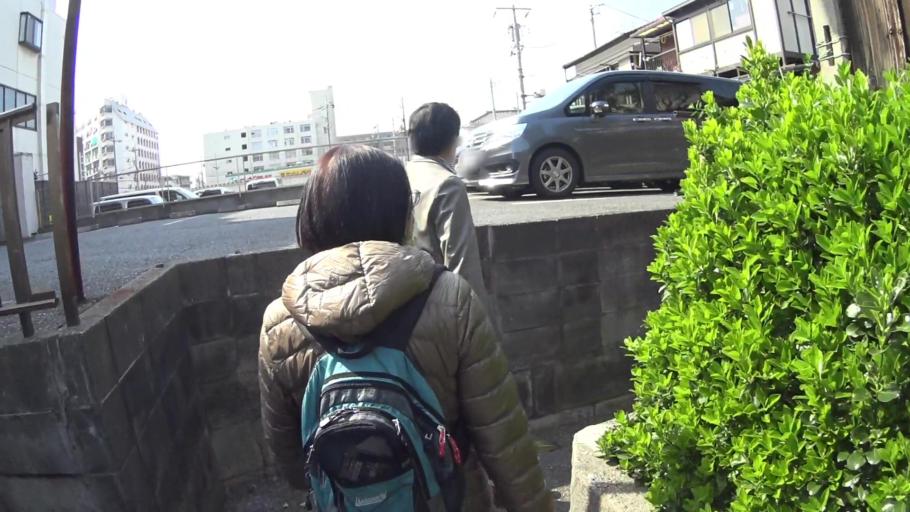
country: JP
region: Chiba
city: Funabashi
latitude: 35.6938
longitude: 140.0219
